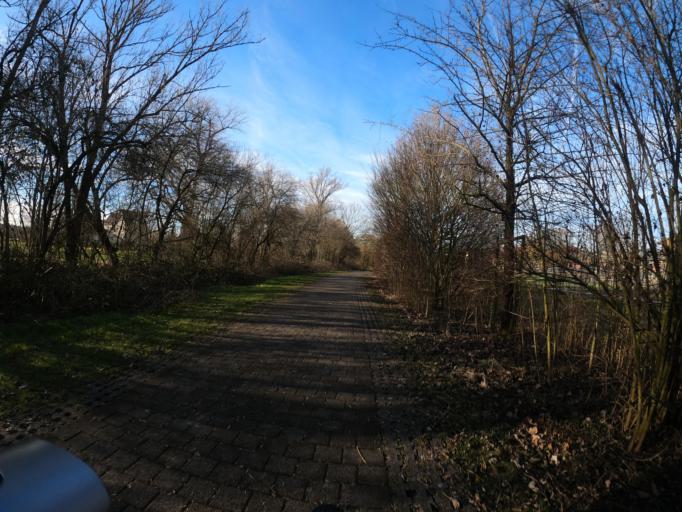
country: DE
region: Baden-Wuerttemberg
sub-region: Regierungsbezirk Stuttgart
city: Wernau
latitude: 48.6638
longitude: 9.4108
